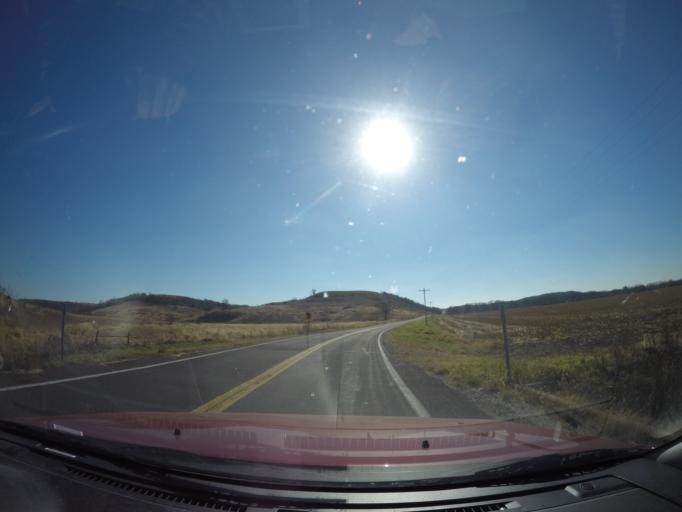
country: US
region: Kansas
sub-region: Geary County
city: Grandview Plaza
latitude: 39.0065
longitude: -96.7308
